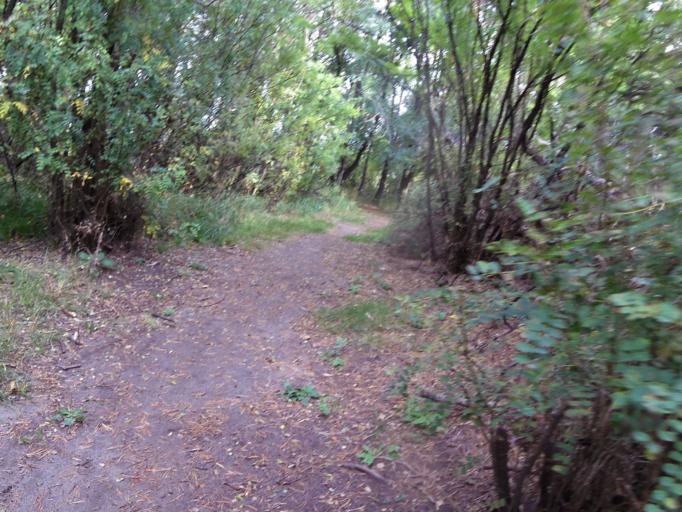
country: US
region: North Dakota
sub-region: Pembina County
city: Cavalier
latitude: 48.7814
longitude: -97.7491
